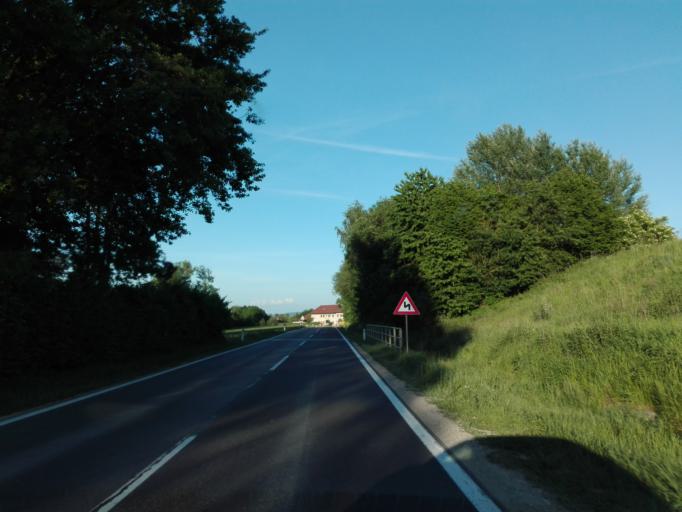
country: AT
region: Upper Austria
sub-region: Politischer Bezirk Urfahr-Umgebung
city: Feldkirchen an der Donau
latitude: 48.3061
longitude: 13.9928
